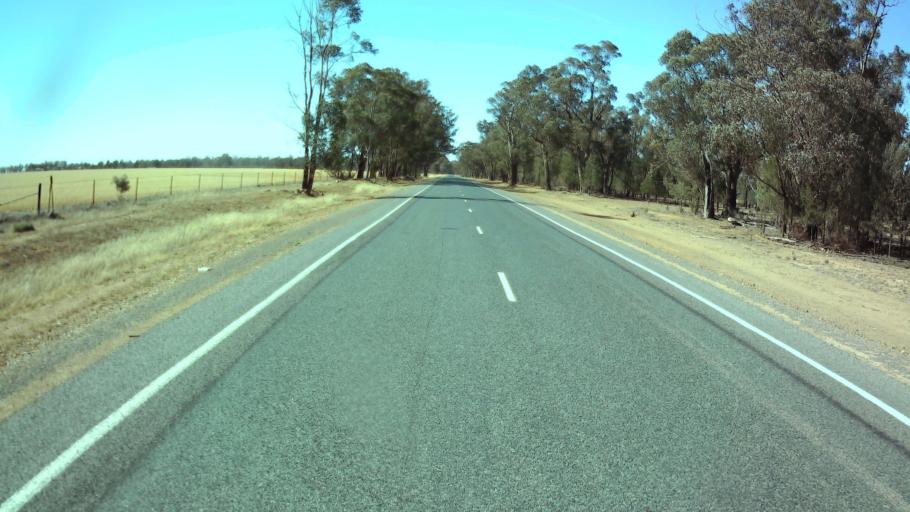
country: AU
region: New South Wales
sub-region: Weddin
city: Grenfell
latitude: -33.7400
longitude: 148.0887
